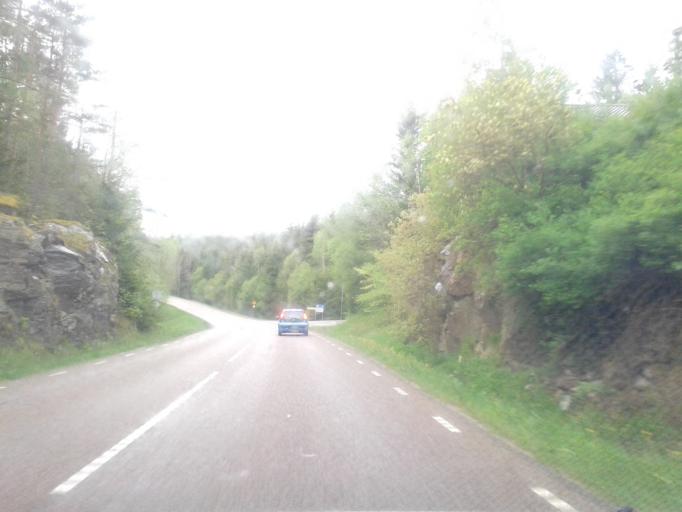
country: SE
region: Vaestra Goetaland
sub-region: Lilla Edets Kommun
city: Lodose
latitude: 58.0779
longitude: 12.1247
